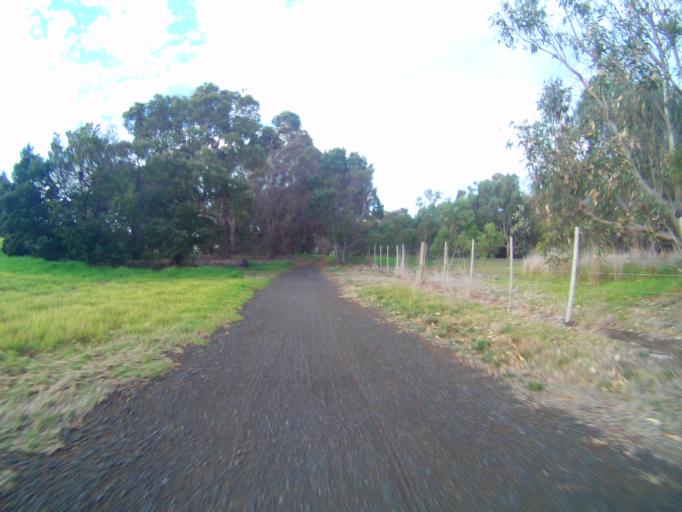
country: AU
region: Victoria
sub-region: Queenscliffe
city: Queenscliff
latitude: -38.2575
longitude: 144.6126
